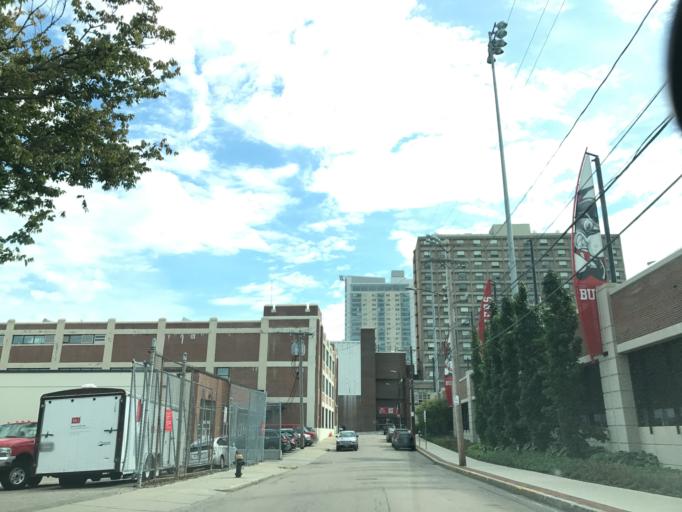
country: US
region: Massachusetts
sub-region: Norfolk County
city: Brookline
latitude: 42.3540
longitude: -71.1223
